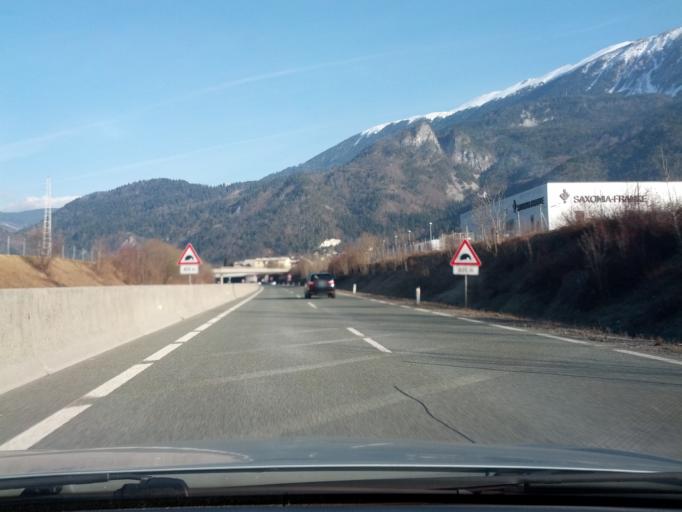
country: SI
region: Zirovnica
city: Zirovnica
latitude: 46.4008
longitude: 14.1312
